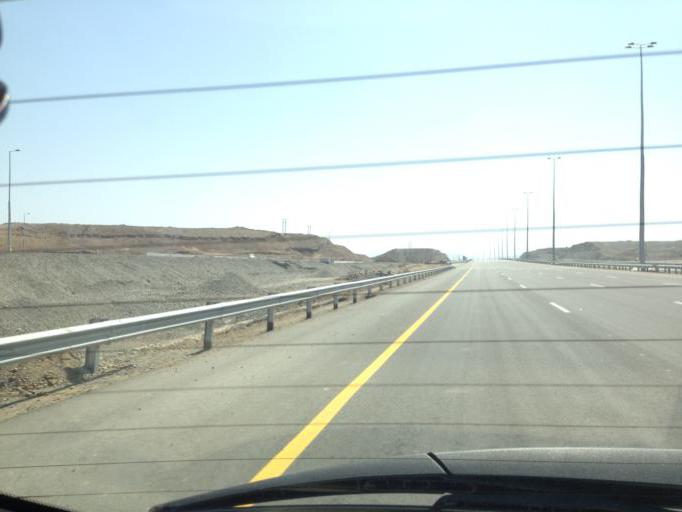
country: OM
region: Al Batinah
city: Rustaq
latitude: 23.5483
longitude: 57.5108
